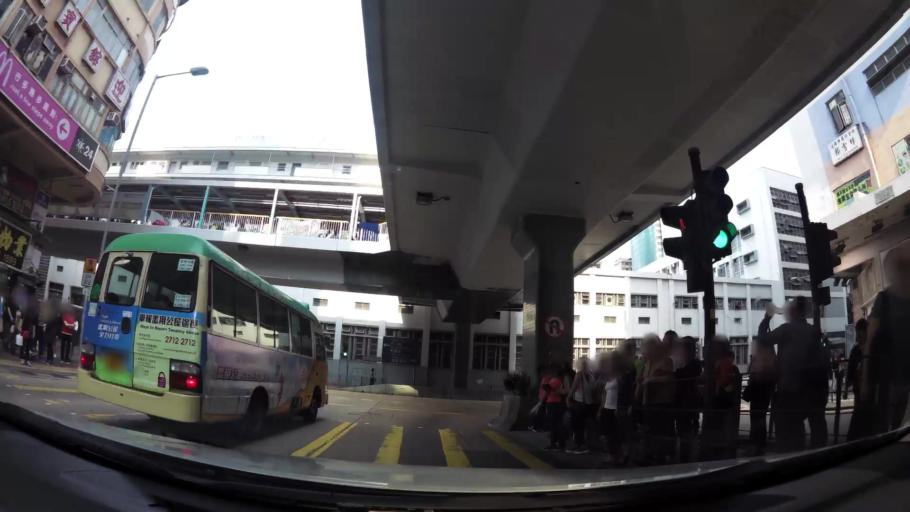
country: HK
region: Kowloon City
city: Kowloon
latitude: 22.3212
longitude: 114.1710
